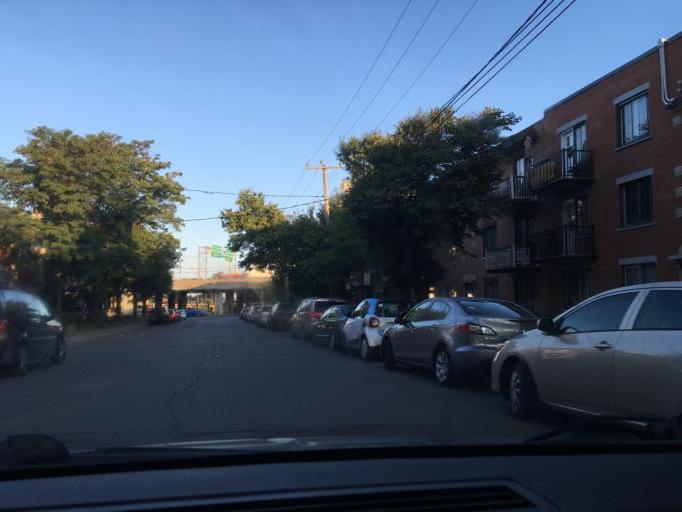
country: CA
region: Quebec
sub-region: Montreal
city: Saint-Leonard
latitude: 45.5529
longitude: -73.6221
